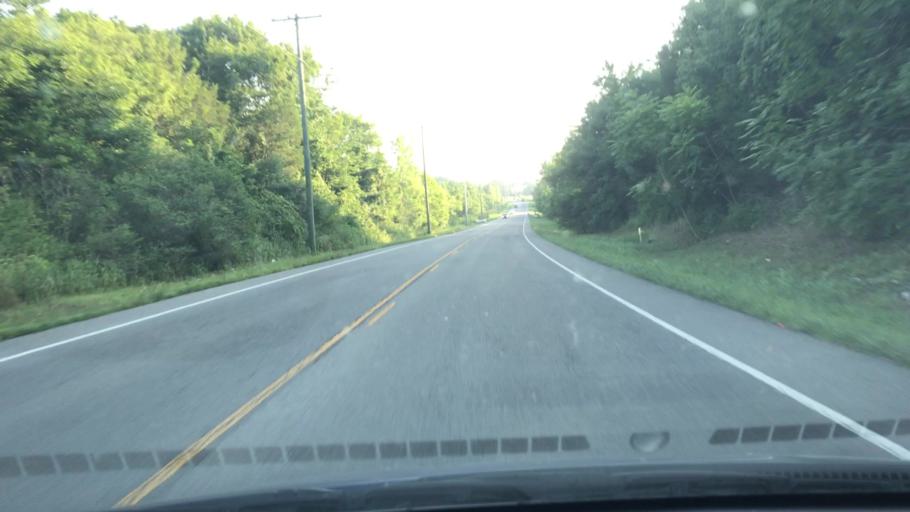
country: US
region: Tennessee
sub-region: Rutherford County
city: La Vergne
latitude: 35.9984
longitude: -86.6238
